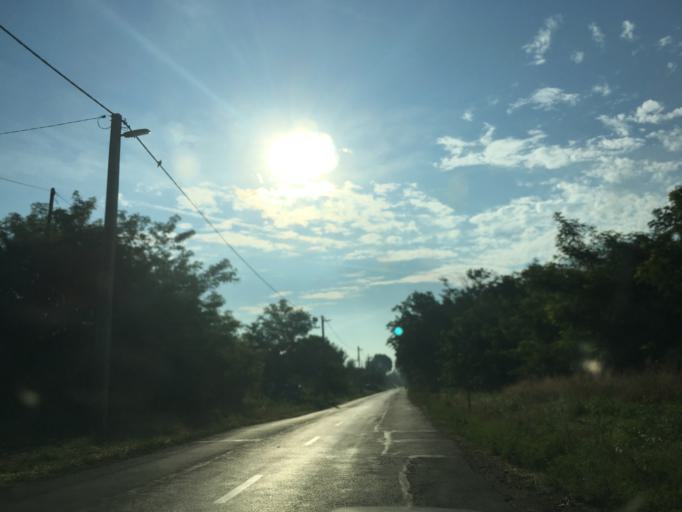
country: HU
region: Hajdu-Bihar
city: Hajdusamson
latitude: 47.5644
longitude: 21.7521
